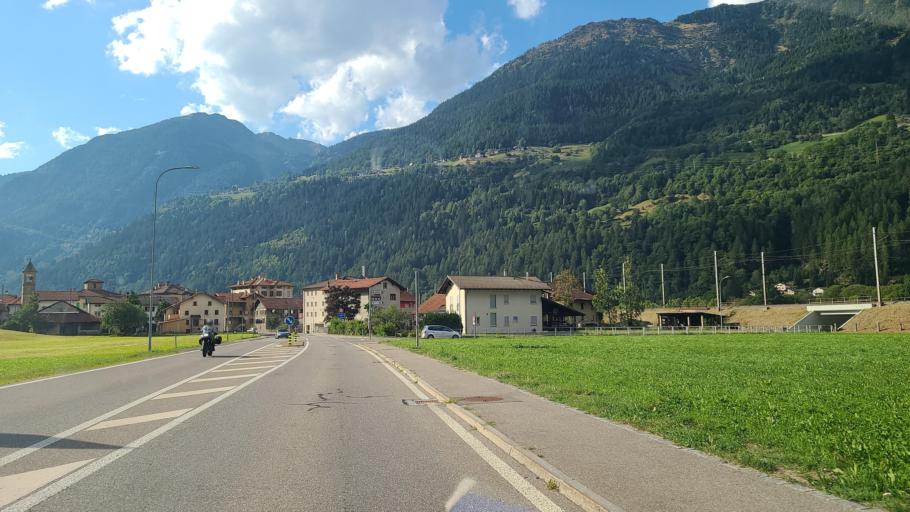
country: CH
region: Ticino
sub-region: Leventina District
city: Airolo
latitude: 46.5066
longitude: 8.7051
